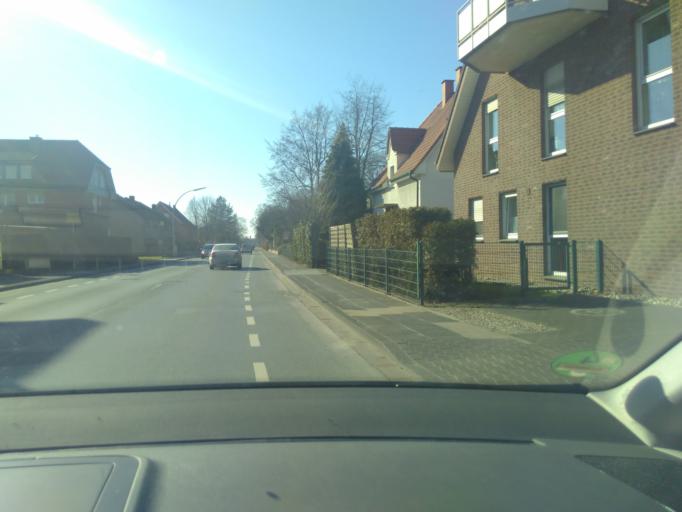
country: DE
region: North Rhine-Westphalia
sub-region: Regierungsbezirk Detmold
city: Rheda-Wiedenbruck
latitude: 51.8407
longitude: 8.3104
